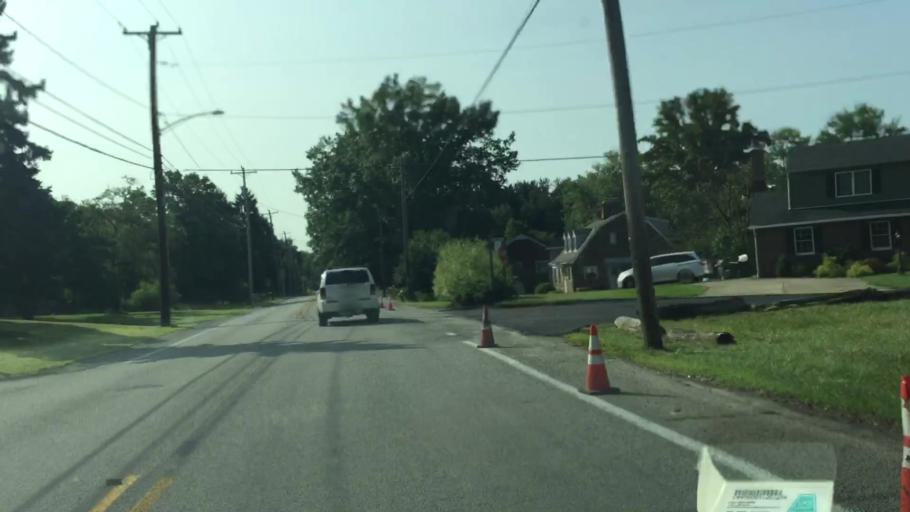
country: US
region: Pennsylvania
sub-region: Allegheny County
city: Fox Chapel
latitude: 40.5172
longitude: -79.8612
